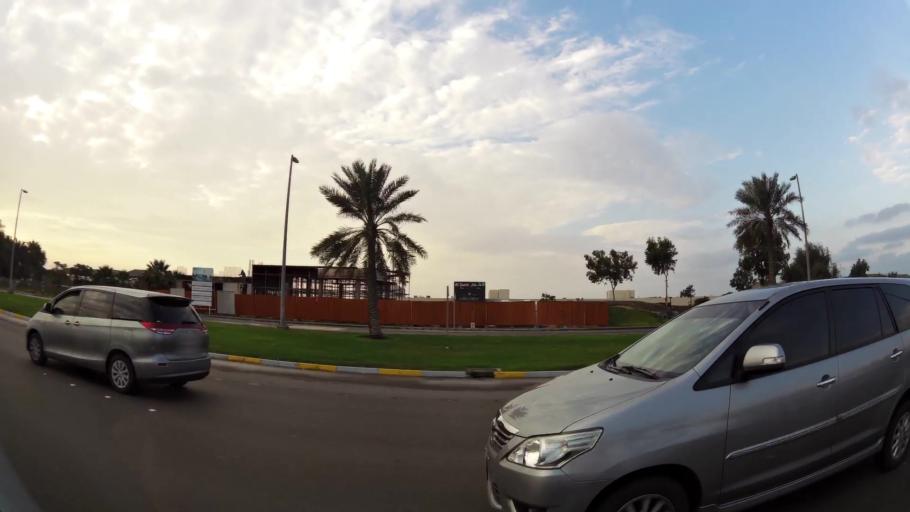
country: AE
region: Abu Dhabi
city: Abu Dhabi
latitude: 24.4250
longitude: 54.4076
